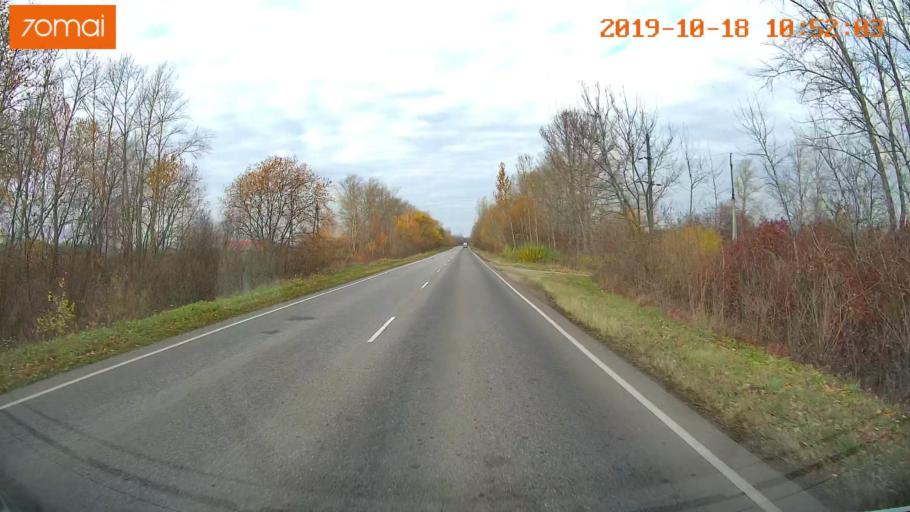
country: RU
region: Tula
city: Yepifan'
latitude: 53.7619
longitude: 38.6578
